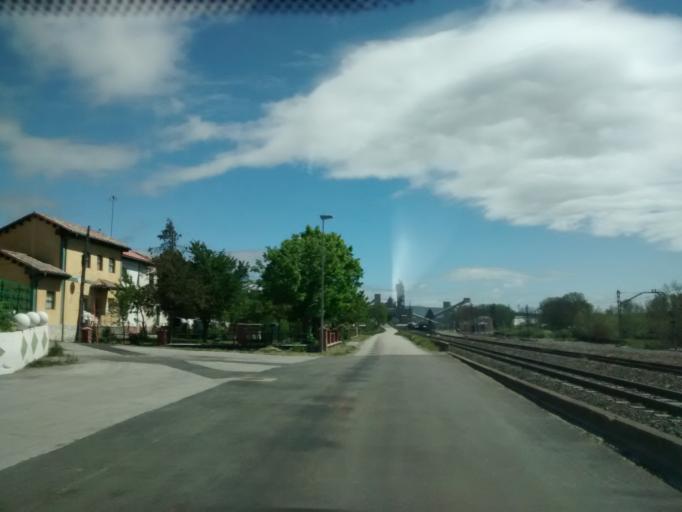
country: ES
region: Cantabria
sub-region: Provincia de Cantabria
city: Mataporquera
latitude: 42.8676
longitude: -4.1722
